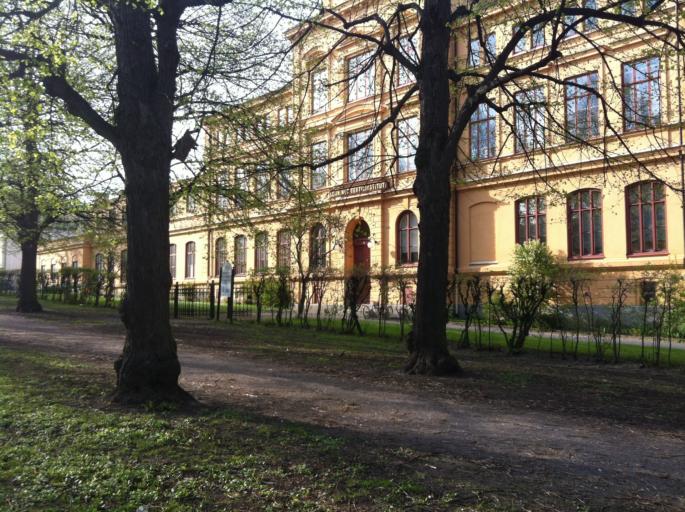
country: SE
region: OEstergoetland
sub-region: Norrkopings Kommun
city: Norrkoping
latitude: 58.5851
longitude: 16.1798
